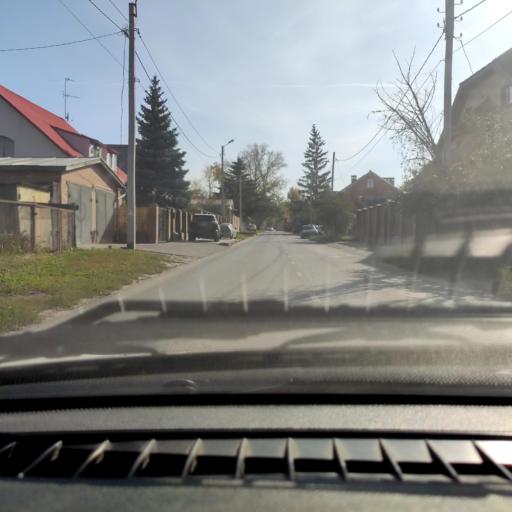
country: RU
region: Samara
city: Tol'yatti
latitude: 53.5144
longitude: 49.3996
